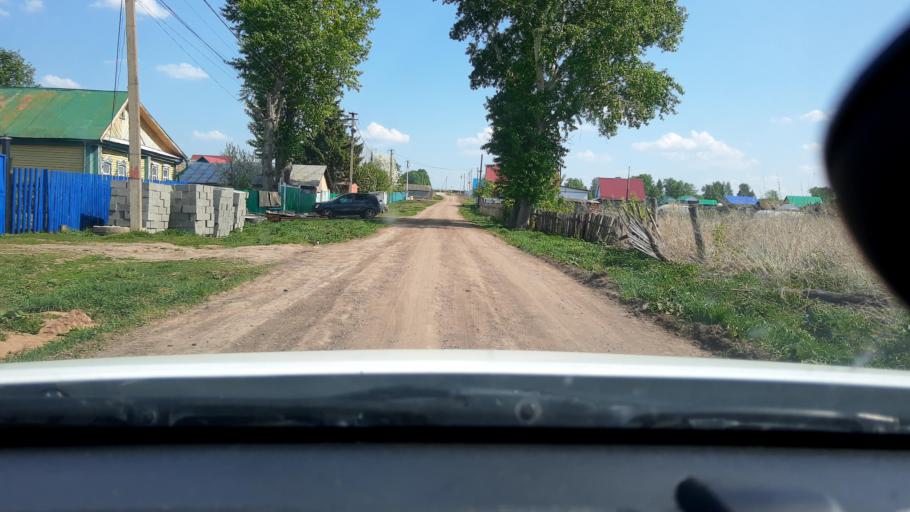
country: RU
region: Bashkortostan
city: Asanovo
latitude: 54.8445
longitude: 55.4552
